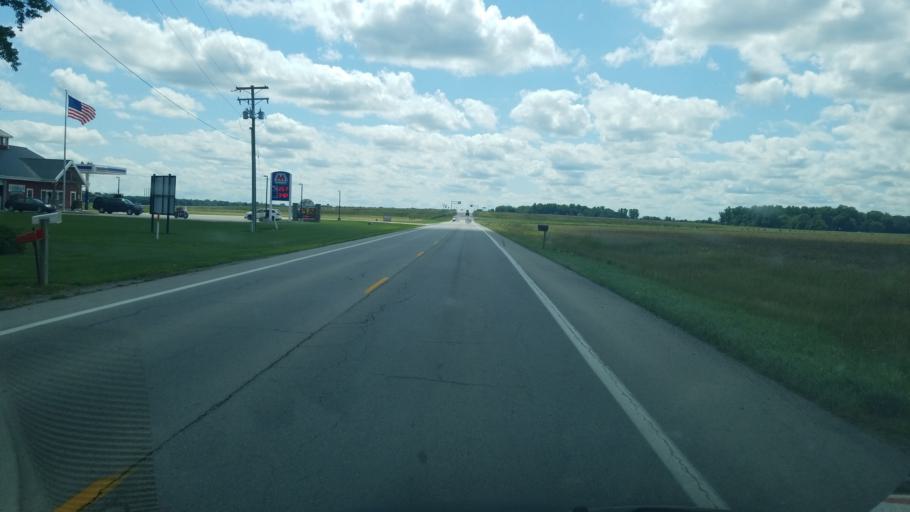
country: US
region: Ohio
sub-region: Henry County
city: Liberty Center
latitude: 41.4351
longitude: -84.0089
